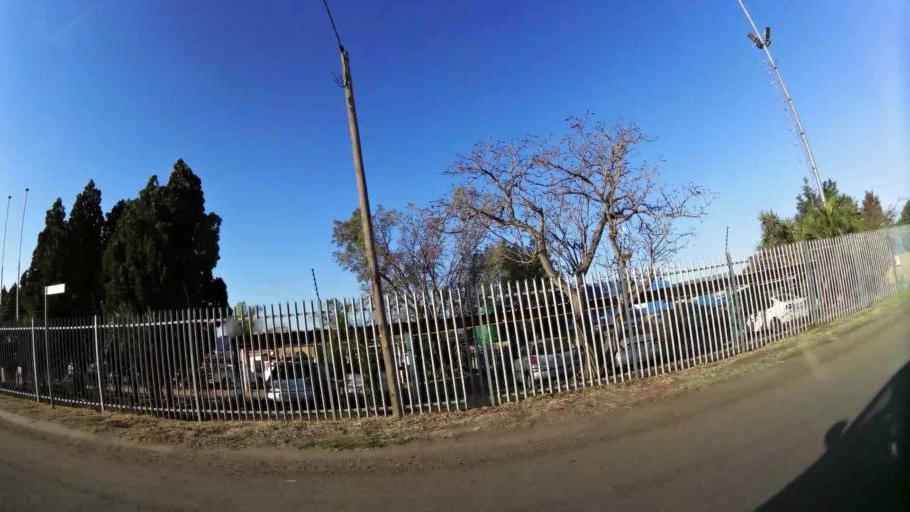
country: ZA
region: North-West
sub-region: Bojanala Platinum District Municipality
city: Rustenburg
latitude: -25.6292
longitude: 27.2188
